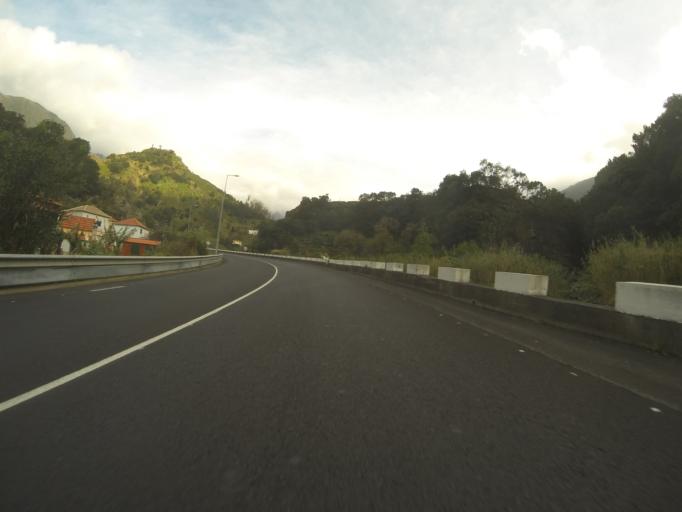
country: PT
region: Madeira
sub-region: Sao Vicente
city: Sao Vicente
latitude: 32.7983
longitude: -17.0422
